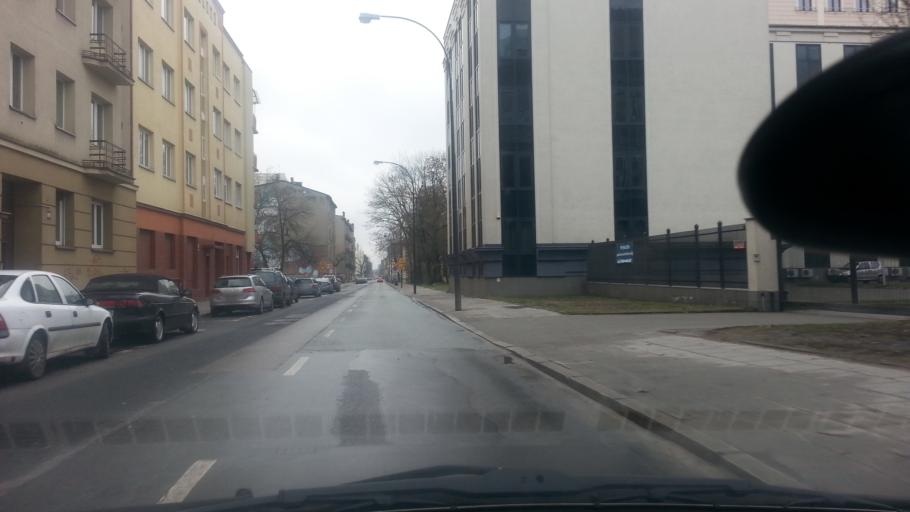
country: PL
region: Lodz Voivodeship
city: Lodz
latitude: 51.7743
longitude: 19.4744
